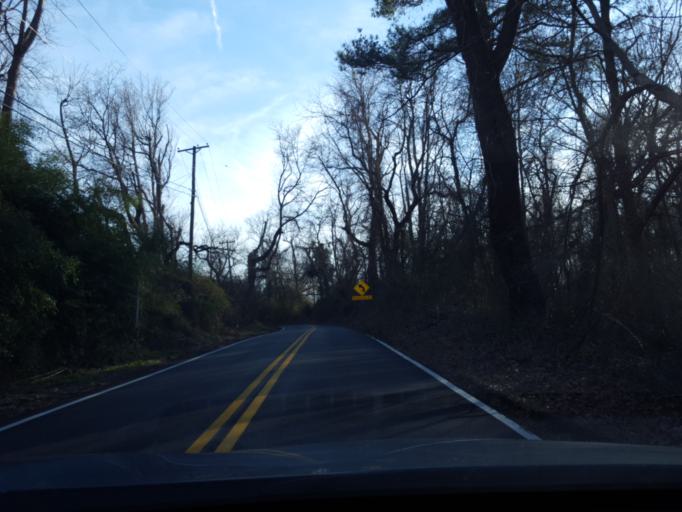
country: US
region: Maryland
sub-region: Anne Arundel County
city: Deale
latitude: 38.7473
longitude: -76.5592
